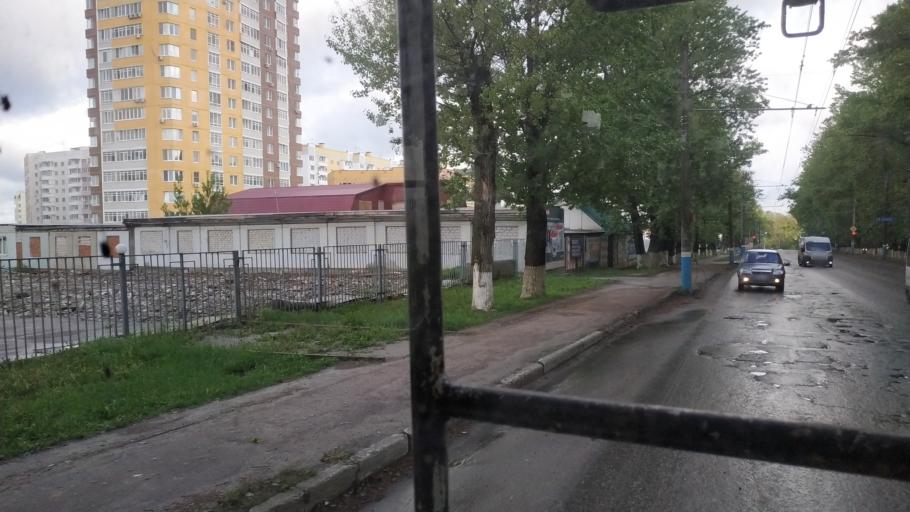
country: RU
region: Brjansk
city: Putevka
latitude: 53.2623
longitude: 34.3245
